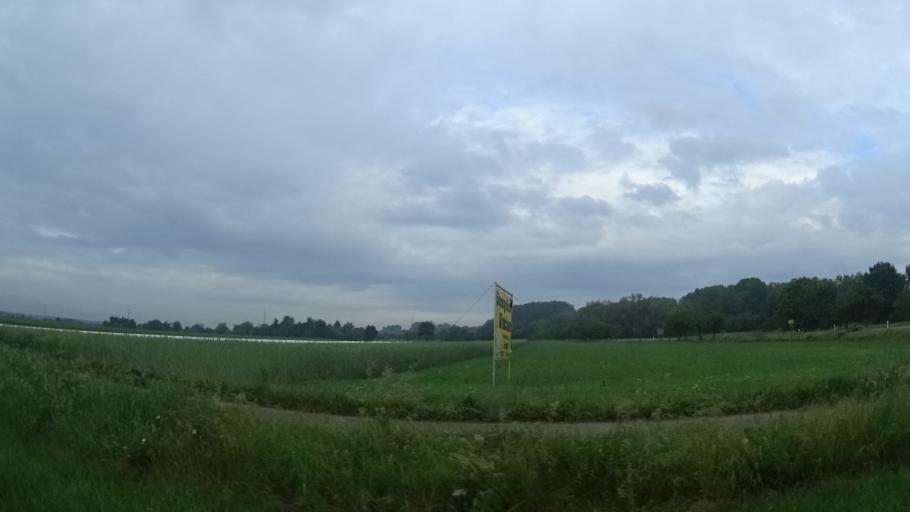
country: DE
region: Rheinland-Pfalz
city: Hordt
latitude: 49.1617
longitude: 8.3245
